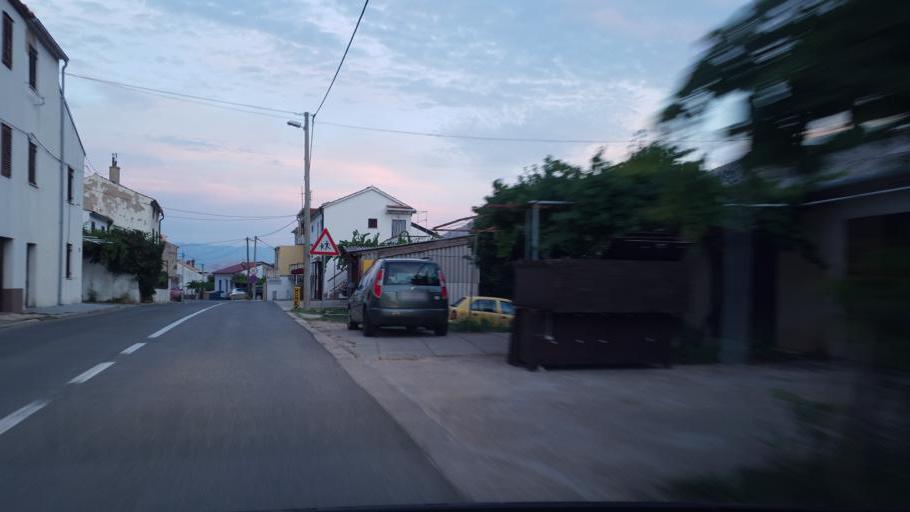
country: HR
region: Primorsko-Goranska
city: Punat
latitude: 44.9964
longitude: 14.7134
